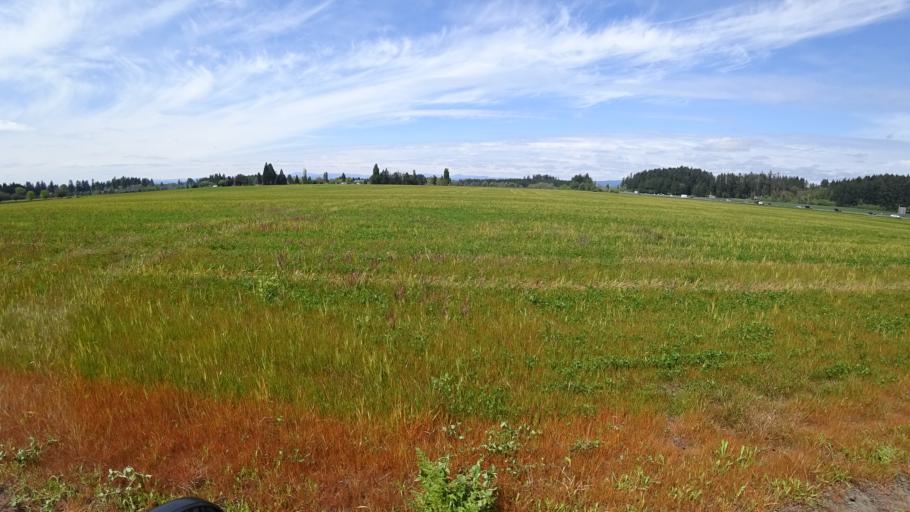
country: US
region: Oregon
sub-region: Washington County
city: North Plains
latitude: 45.5678
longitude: -122.9426
